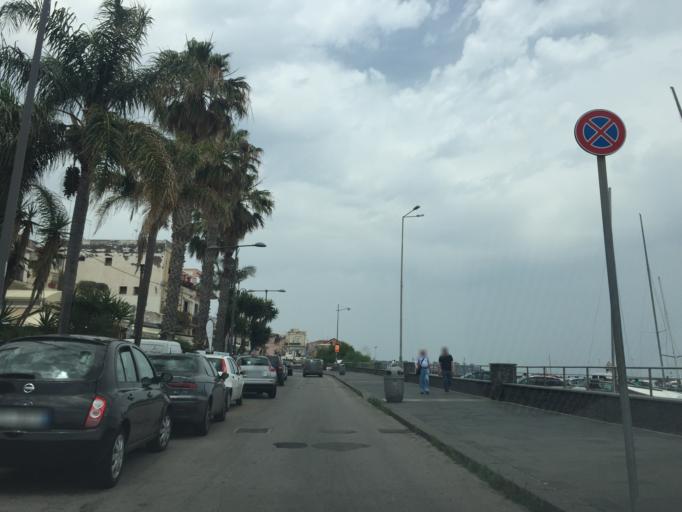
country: IT
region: Sicily
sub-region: Catania
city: Aci Trezza
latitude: 37.5617
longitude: 15.1611
